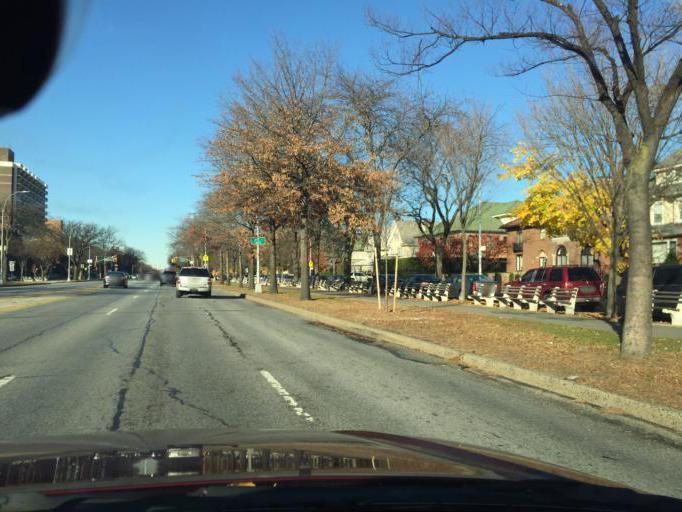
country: US
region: New York
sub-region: Kings County
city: Brooklyn
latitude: 40.6251
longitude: -73.9706
